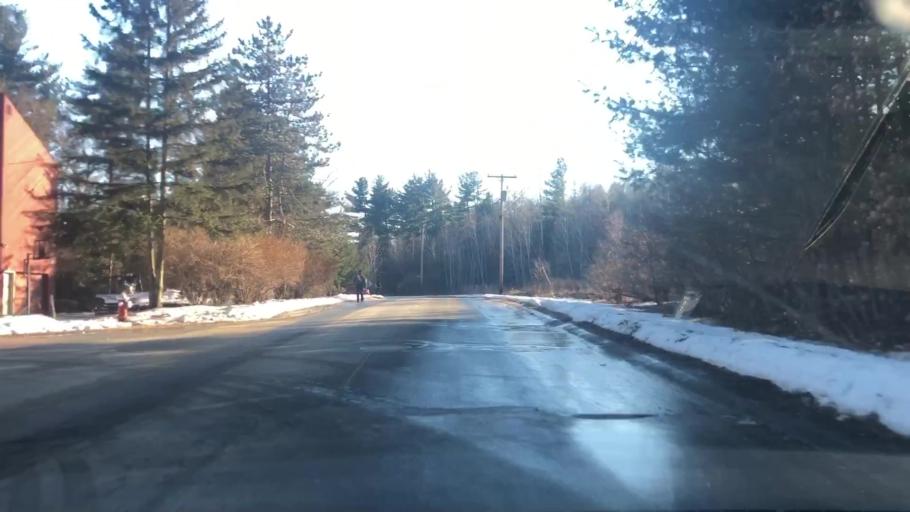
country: US
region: New Hampshire
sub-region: Hillsborough County
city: Milford
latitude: 42.8373
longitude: -71.6811
